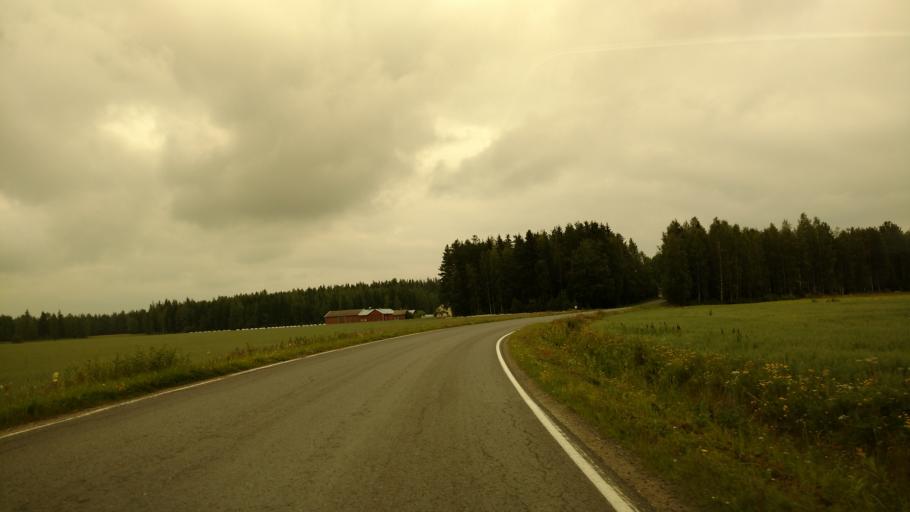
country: FI
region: Varsinais-Suomi
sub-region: Loimaa
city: Koski Tl
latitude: 60.7376
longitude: 23.1926
